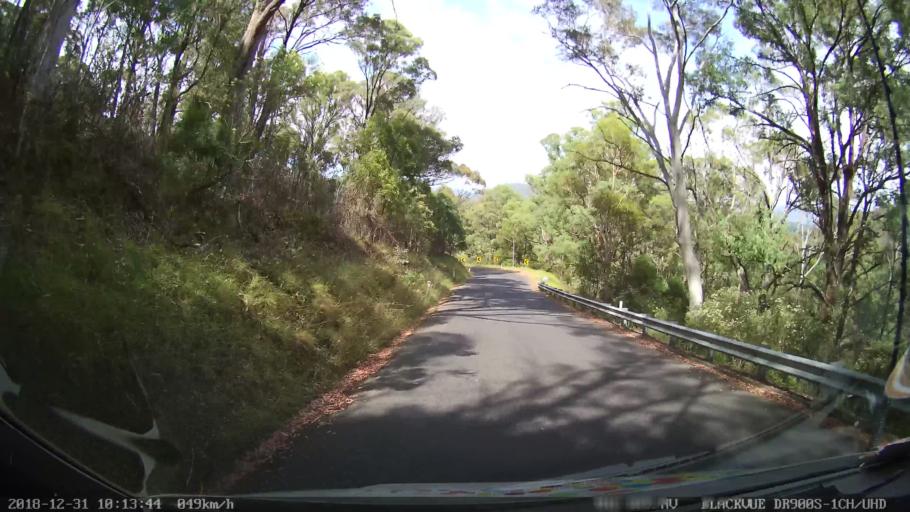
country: AU
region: New South Wales
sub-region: Snowy River
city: Jindabyne
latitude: -36.5390
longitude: 148.1527
